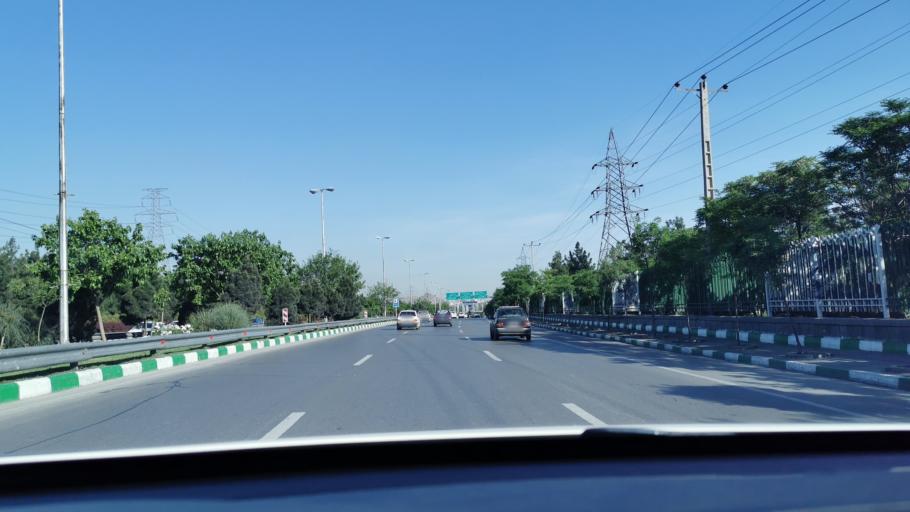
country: IR
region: Razavi Khorasan
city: Mashhad
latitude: 36.2584
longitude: 59.5885
